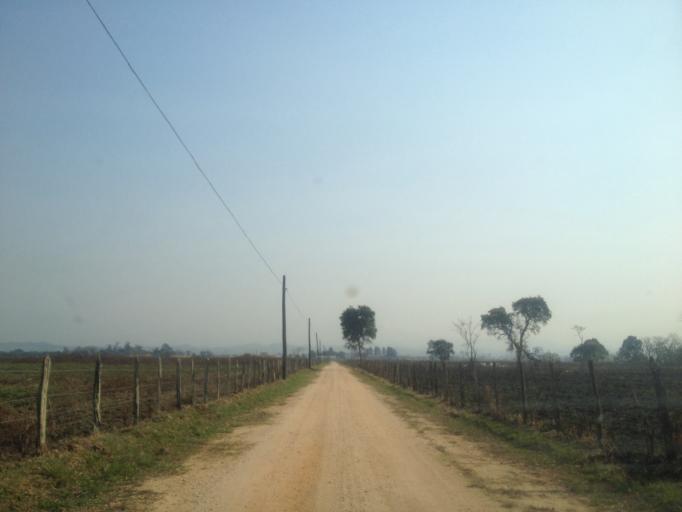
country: BR
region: Rio de Janeiro
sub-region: Porto Real
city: Porto Real
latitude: -22.4614
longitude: -44.3561
